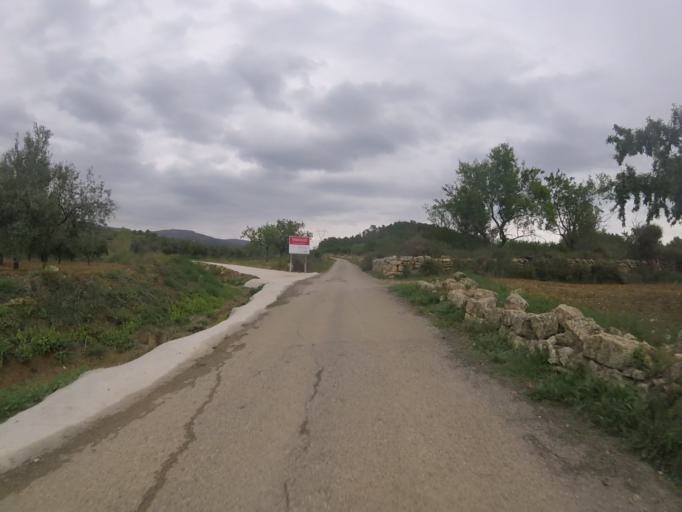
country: ES
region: Valencia
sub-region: Provincia de Castello
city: Sarratella
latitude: 40.2723
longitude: 0.0712
